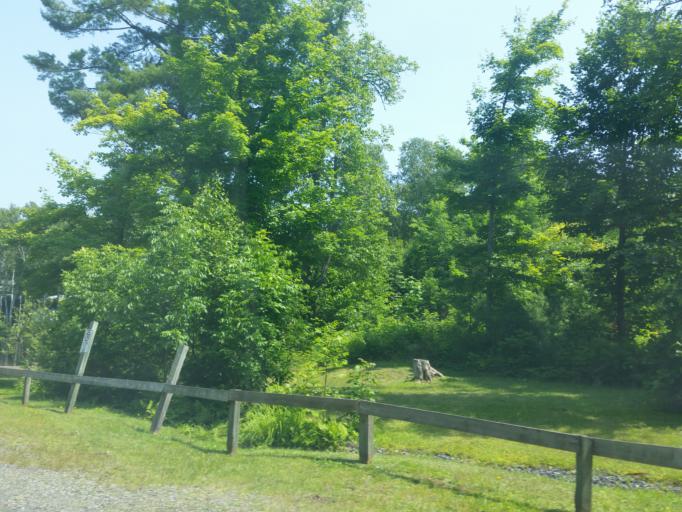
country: CA
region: Ontario
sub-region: Parry Sound District
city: Parry Sound
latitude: 45.4357
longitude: -80.0018
